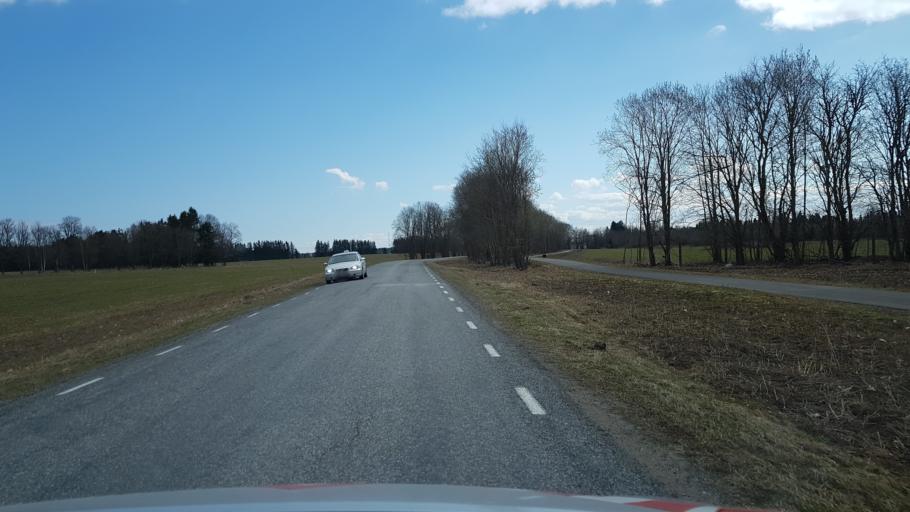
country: EE
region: Laeaene-Virumaa
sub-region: Haljala vald
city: Haljala
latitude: 59.3969
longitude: 26.2825
